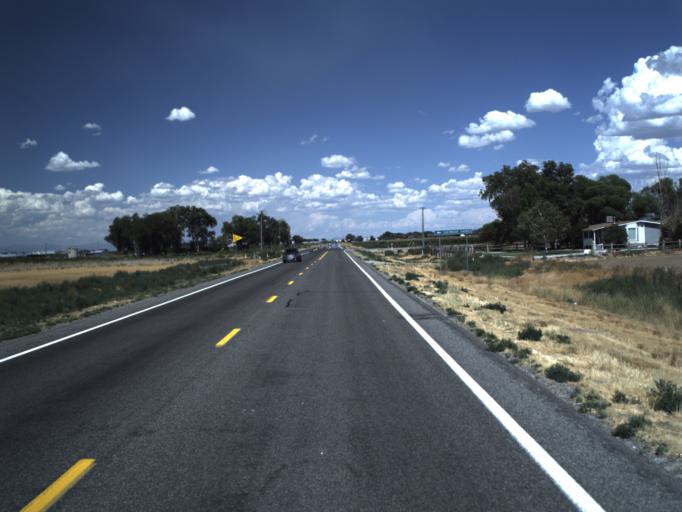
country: US
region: Utah
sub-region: Millard County
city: Delta
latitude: 39.3362
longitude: -112.6077
